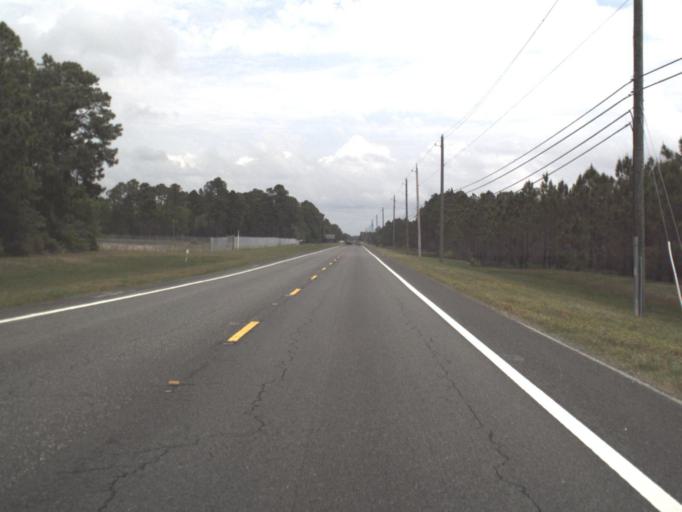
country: US
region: Florida
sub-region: Santa Rosa County
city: Oriole Beach
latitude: 30.4651
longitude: -87.0891
